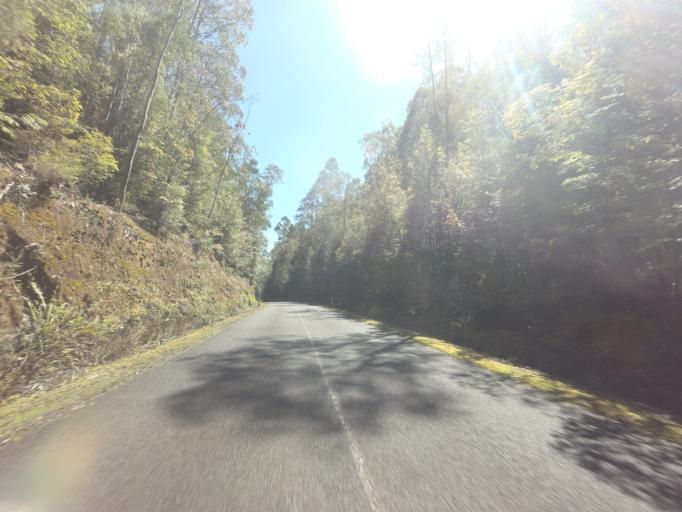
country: AU
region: Tasmania
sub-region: Huon Valley
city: Geeveston
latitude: -42.8252
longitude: 146.3157
